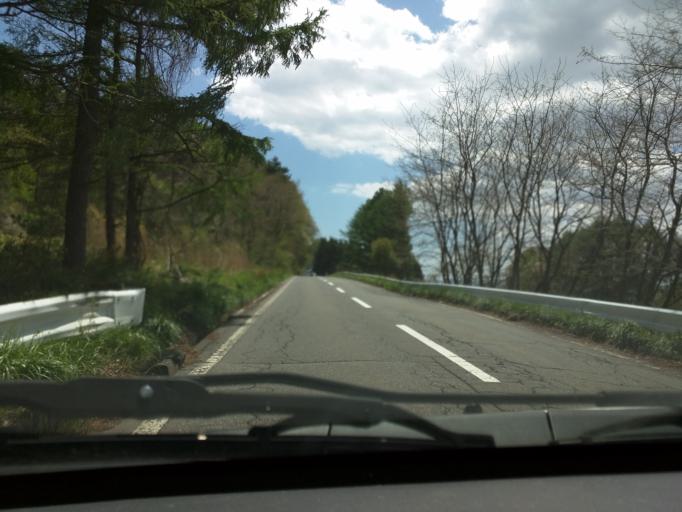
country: JP
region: Nagano
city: Nagano-shi
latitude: 36.6882
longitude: 138.1581
